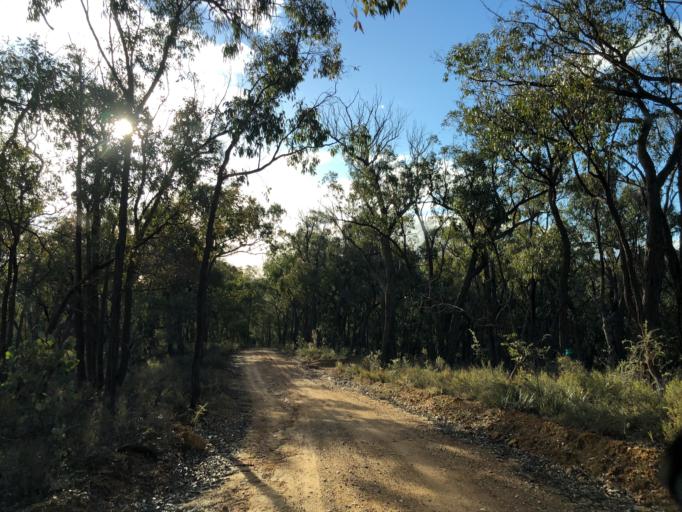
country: AU
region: Victoria
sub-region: Mount Alexander
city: Castlemaine
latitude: -37.2265
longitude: 144.2681
